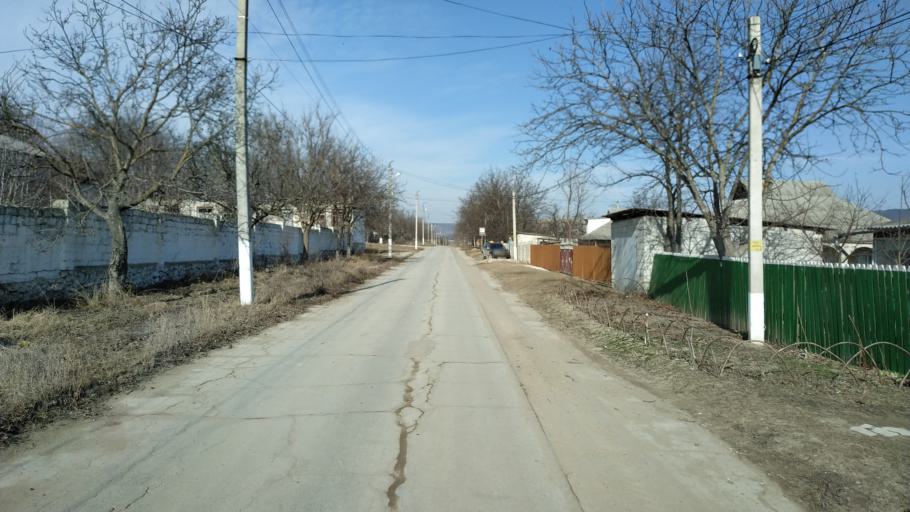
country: MD
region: Nisporeni
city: Nisporeni
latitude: 47.0655
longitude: 28.1730
